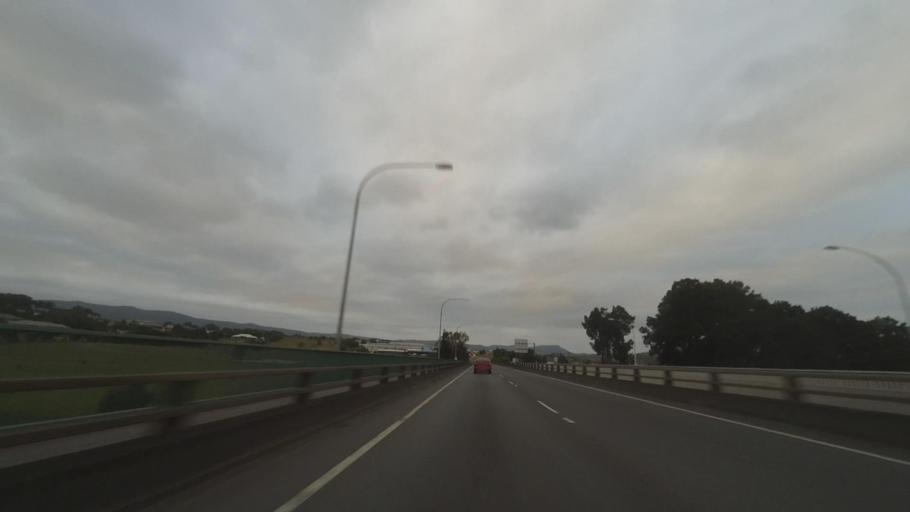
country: AU
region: New South Wales
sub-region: Shellharbour
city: Albion Park Rail
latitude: -34.5472
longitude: 150.7850
